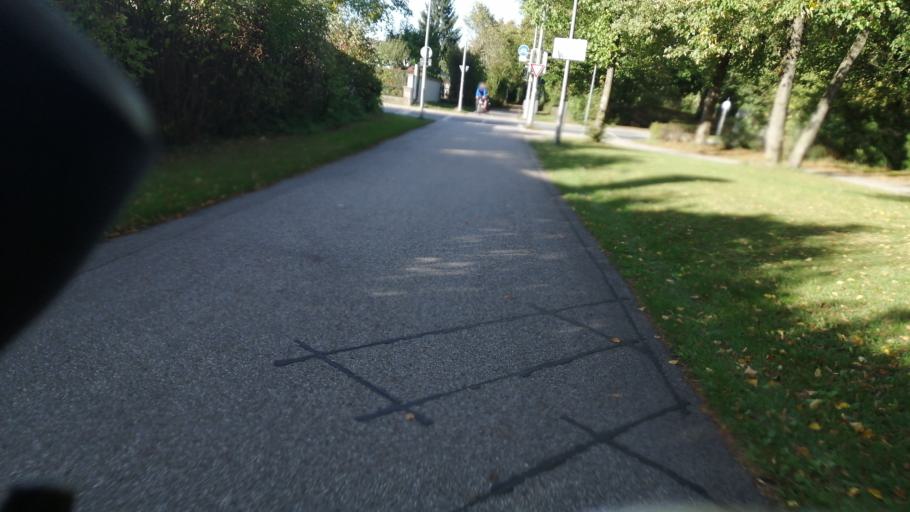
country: DE
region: Bavaria
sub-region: Upper Bavaria
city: Oberschleissheim
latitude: 48.1960
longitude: 11.5755
